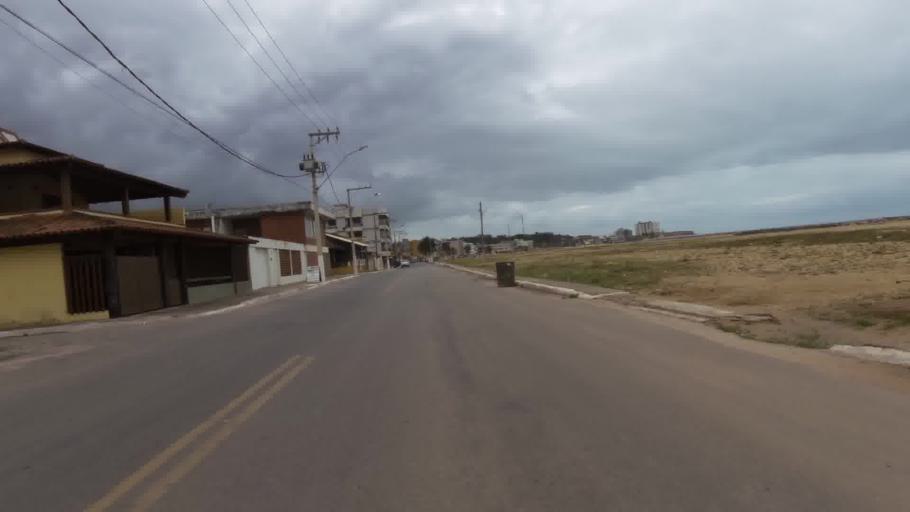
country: BR
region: Espirito Santo
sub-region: Marataizes
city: Marataizes
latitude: -21.0484
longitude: -40.8303
